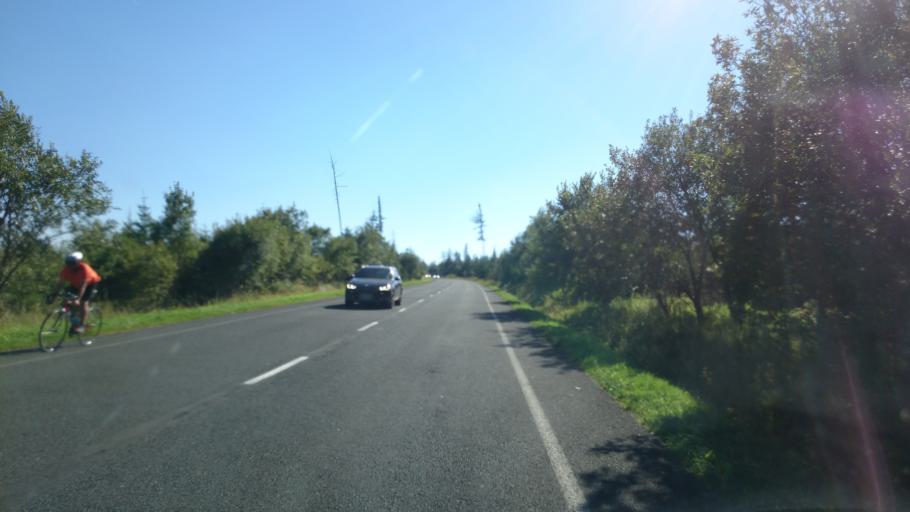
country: SK
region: Presovsky
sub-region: Okres Poprad
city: Zdiar
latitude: 49.1995
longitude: 20.3053
